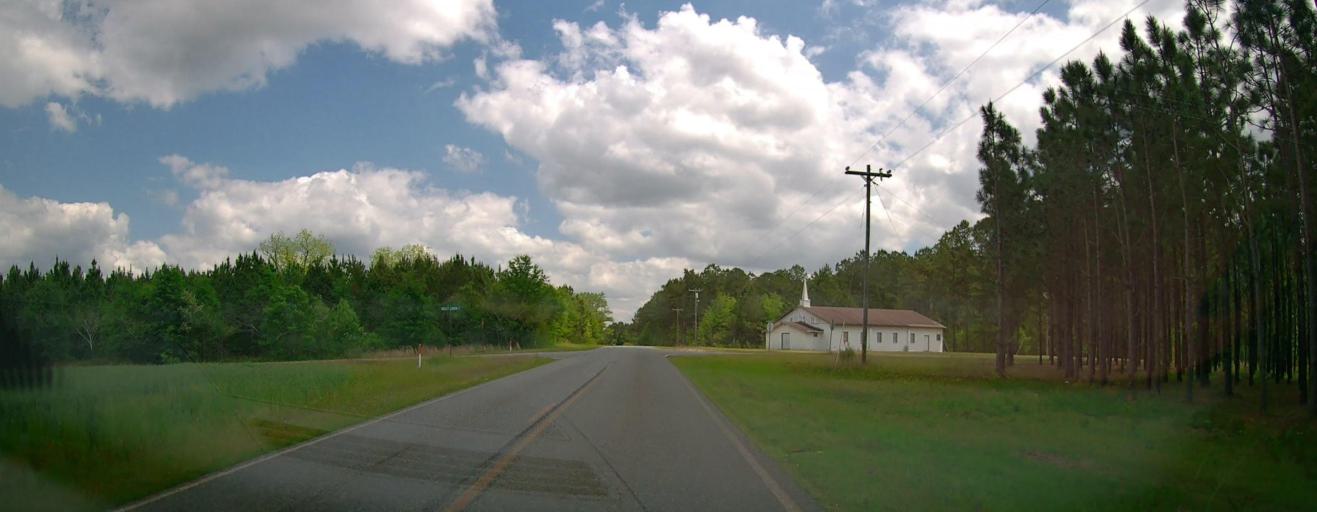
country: US
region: Georgia
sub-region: Laurens County
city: Dublin
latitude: 32.5929
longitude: -83.0251
